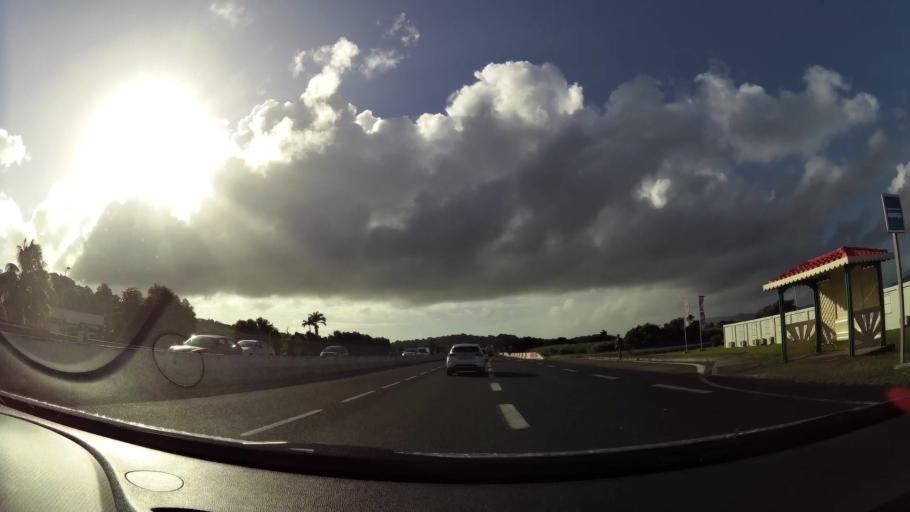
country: MQ
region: Martinique
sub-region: Martinique
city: Ducos
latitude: 14.5934
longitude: -60.9838
